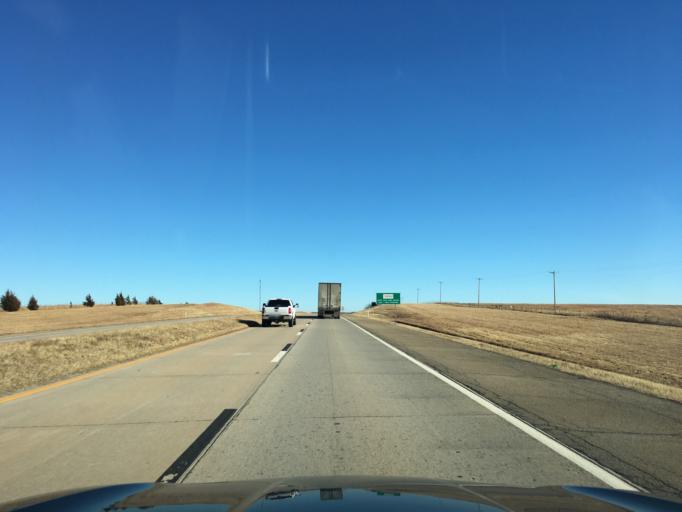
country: US
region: Oklahoma
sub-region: Pawnee County
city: Pawnee
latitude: 36.2247
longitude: -96.7647
